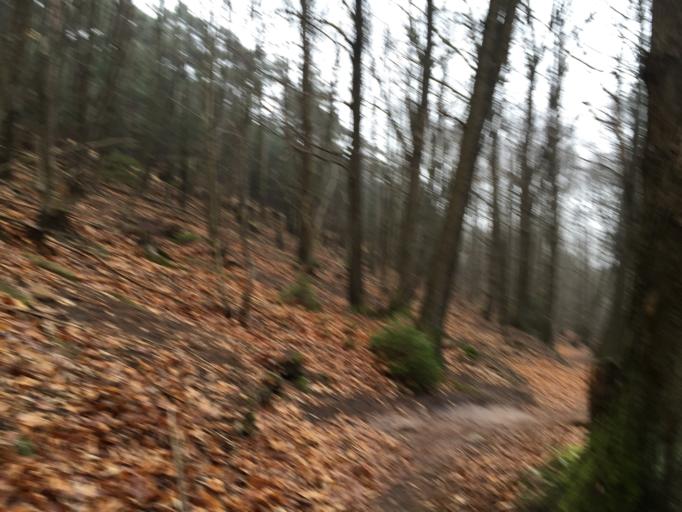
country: DE
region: Rheinland-Pfalz
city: Sankt Martin
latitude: 49.3260
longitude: 8.0940
